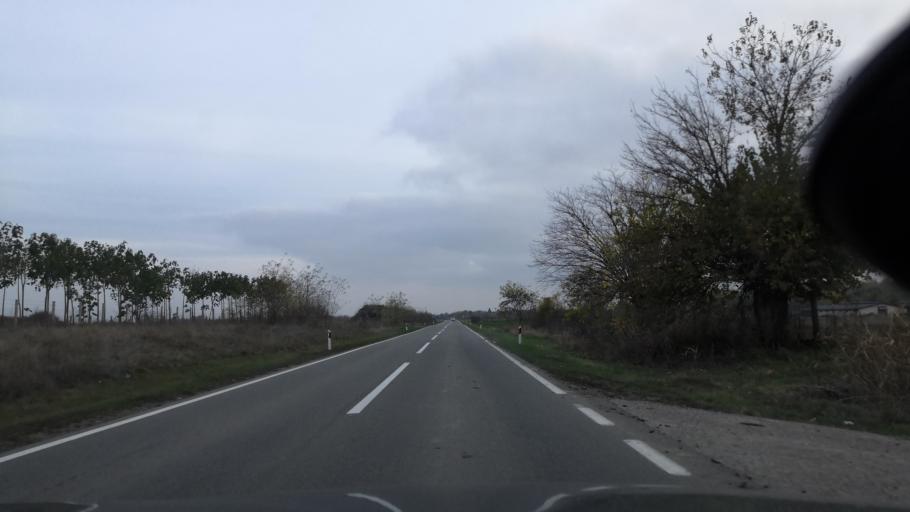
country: RS
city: Sanad
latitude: 45.9927
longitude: 20.1070
